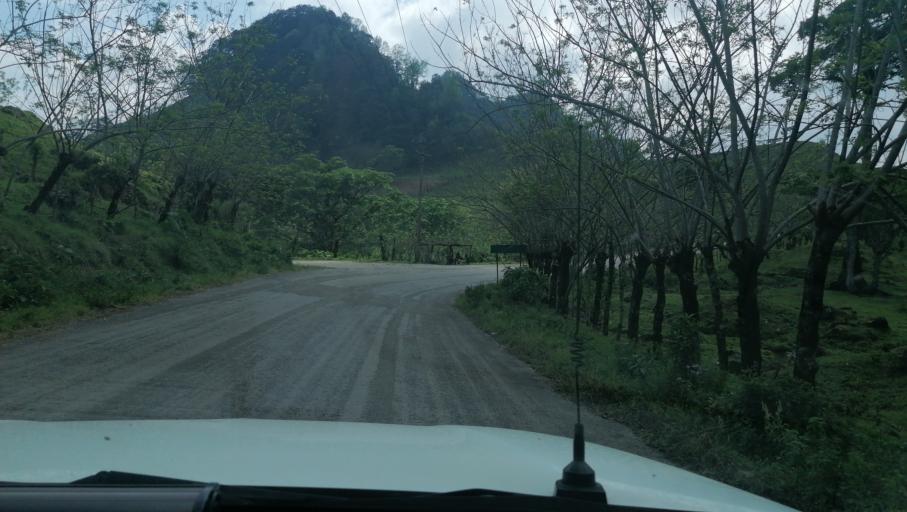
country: MX
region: Chiapas
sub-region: Francisco Leon
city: San Miguel la Sardina
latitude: 17.2510
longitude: -93.2797
